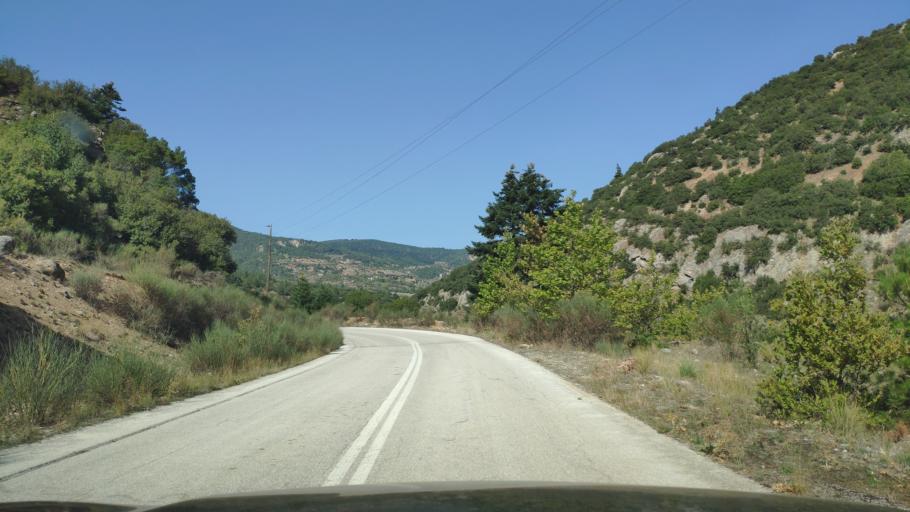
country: GR
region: West Greece
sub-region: Nomos Achaias
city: Aiyira
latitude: 37.9772
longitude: 22.3540
